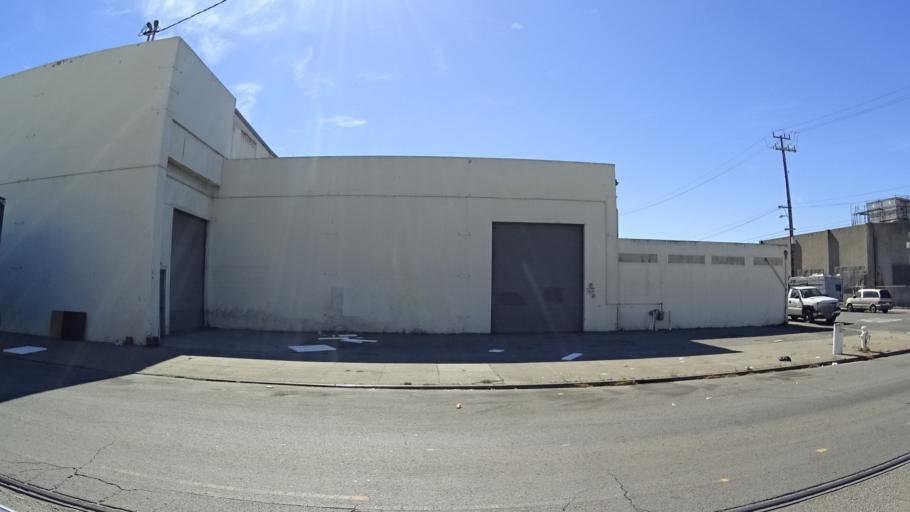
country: US
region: California
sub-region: San Mateo County
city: Brisbane
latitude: 37.7238
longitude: -122.3912
